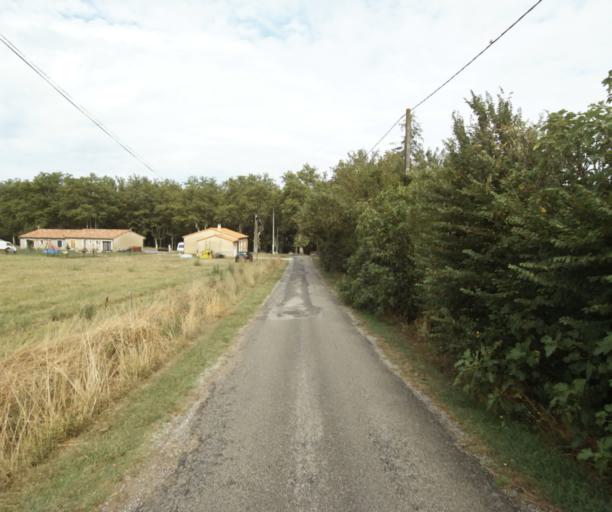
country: FR
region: Midi-Pyrenees
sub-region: Departement de la Haute-Garonne
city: Revel
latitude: 43.4246
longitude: 1.9816
